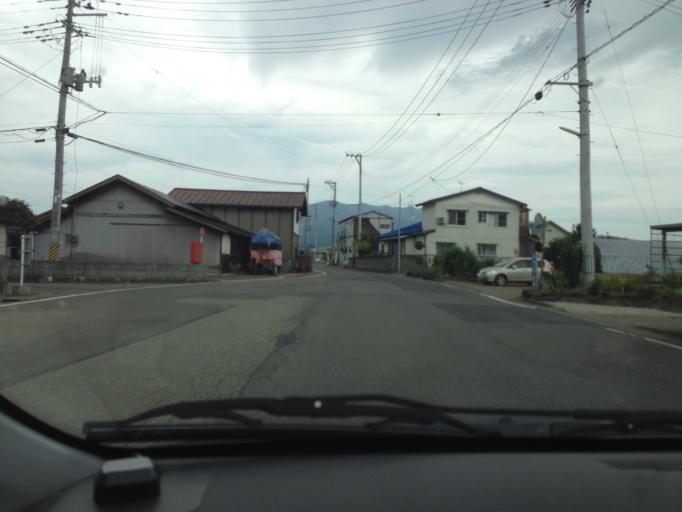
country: JP
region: Fukushima
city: Kitakata
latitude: 37.6312
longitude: 139.8857
